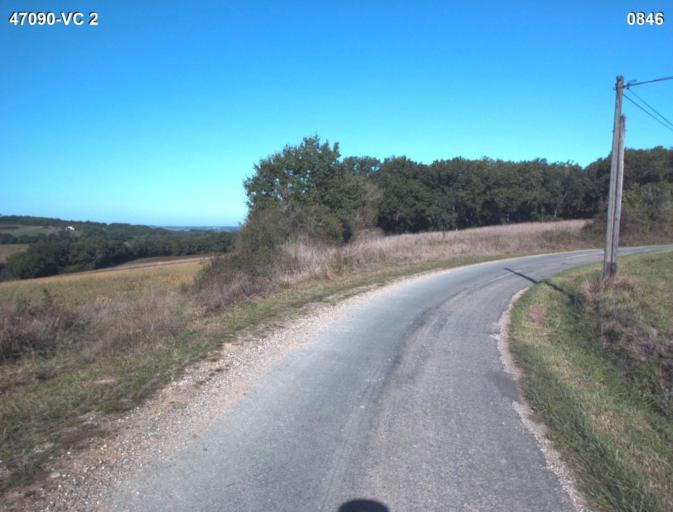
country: FR
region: Aquitaine
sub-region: Departement du Lot-et-Garonne
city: Vianne
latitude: 44.1837
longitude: 0.3654
